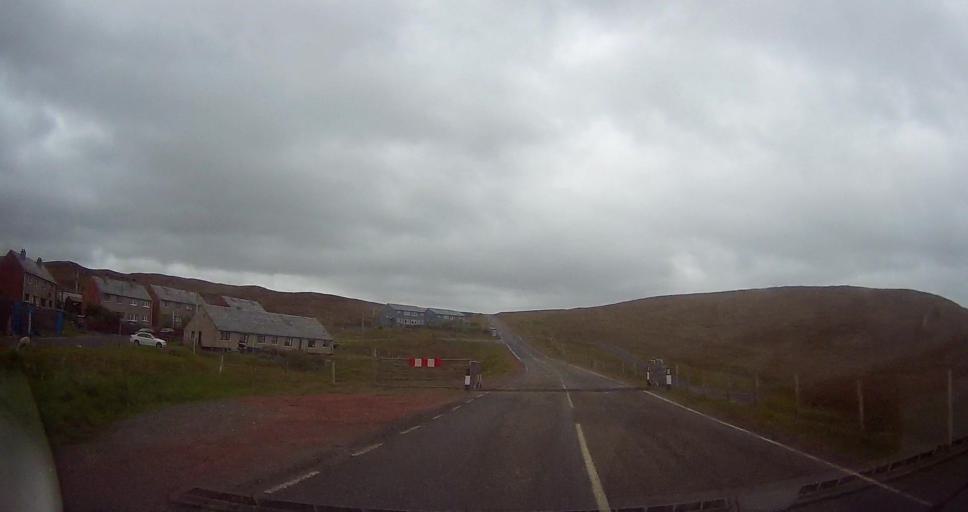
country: GB
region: Scotland
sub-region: Shetland Islands
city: Lerwick
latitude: 60.4888
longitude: -1.4513
